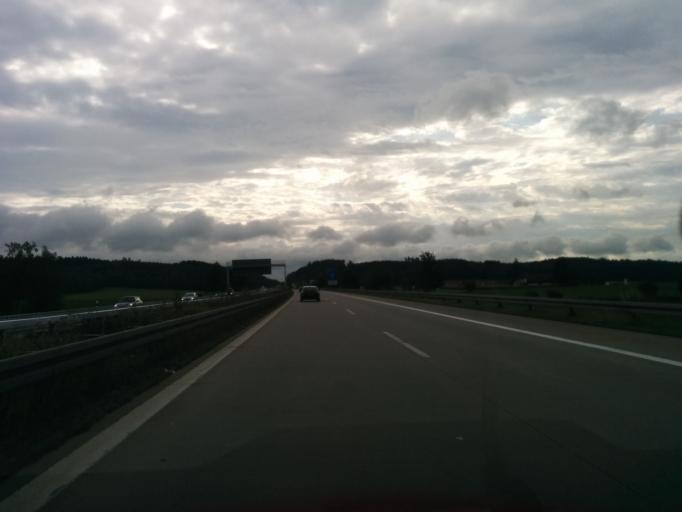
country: DE
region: Bavaria
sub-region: Lower Bavaria
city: Steinach
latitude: 48.9402
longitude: 12.6322
